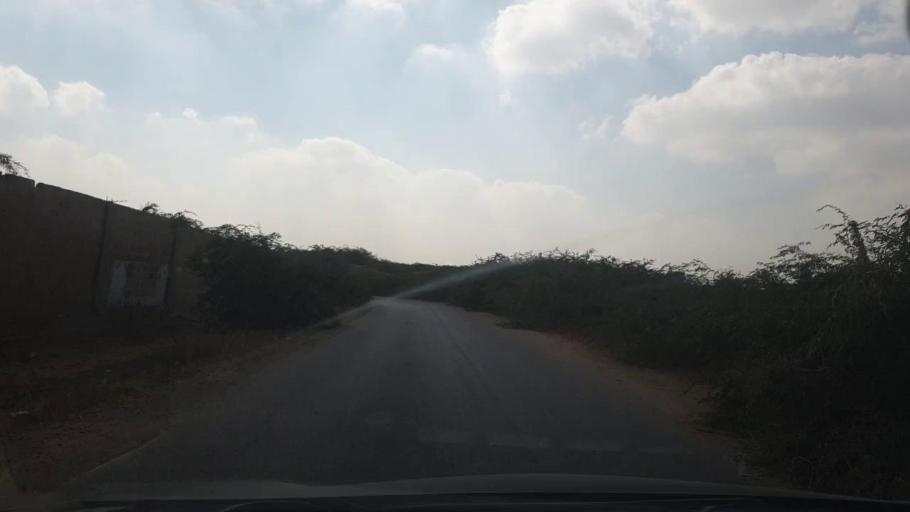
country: PK
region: Sindh
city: Malir Cantonment
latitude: 25.0150
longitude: 67.3527
